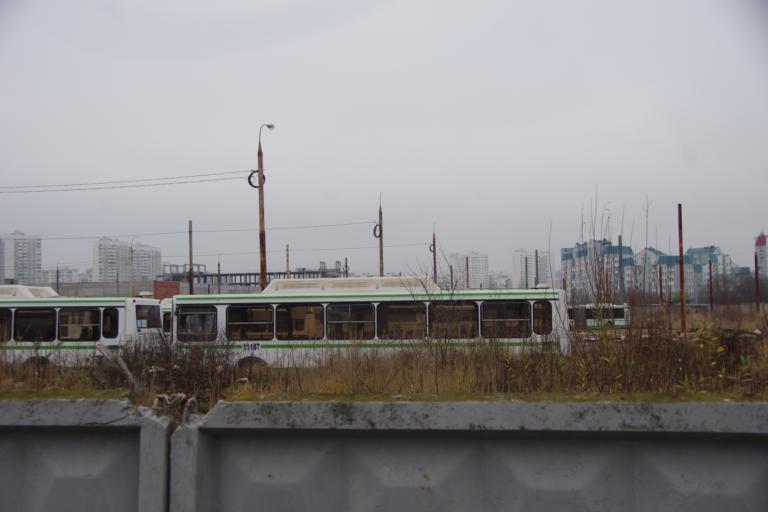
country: RU
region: Moskovskaya
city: Pavshino
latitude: 55.8351
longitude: 37.3485
